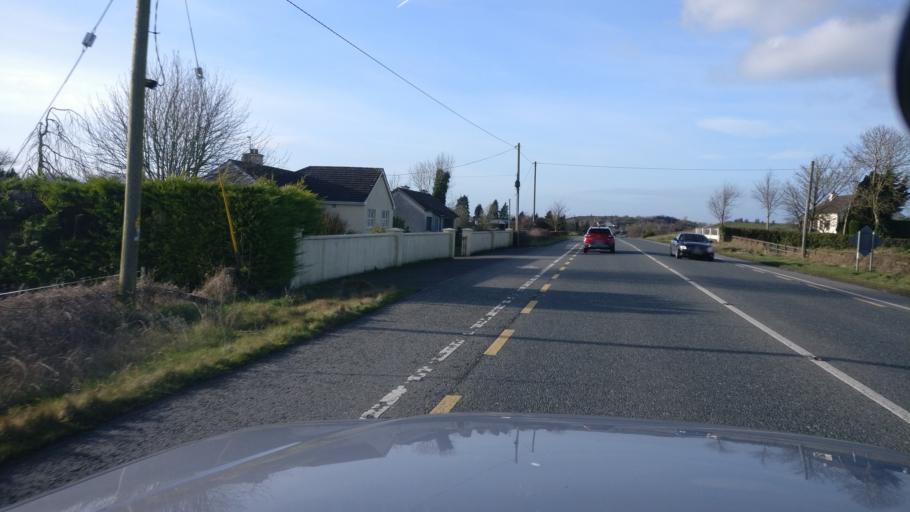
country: IE
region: Leinster
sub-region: Uibh Fhaili
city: Clara
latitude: 53.3197
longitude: -7.5717
